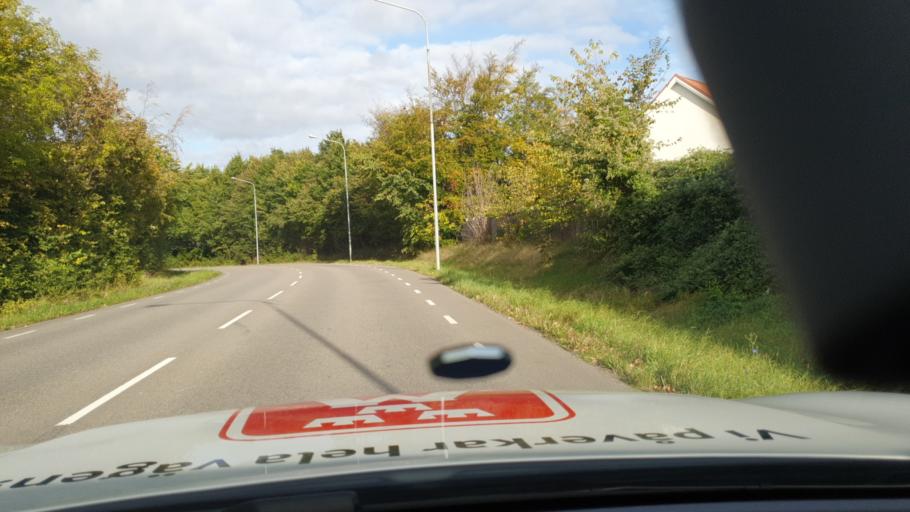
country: SE
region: Skane
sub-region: Vellinge Kommun
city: Vellinge
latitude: 55.4661
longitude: 13.0172
